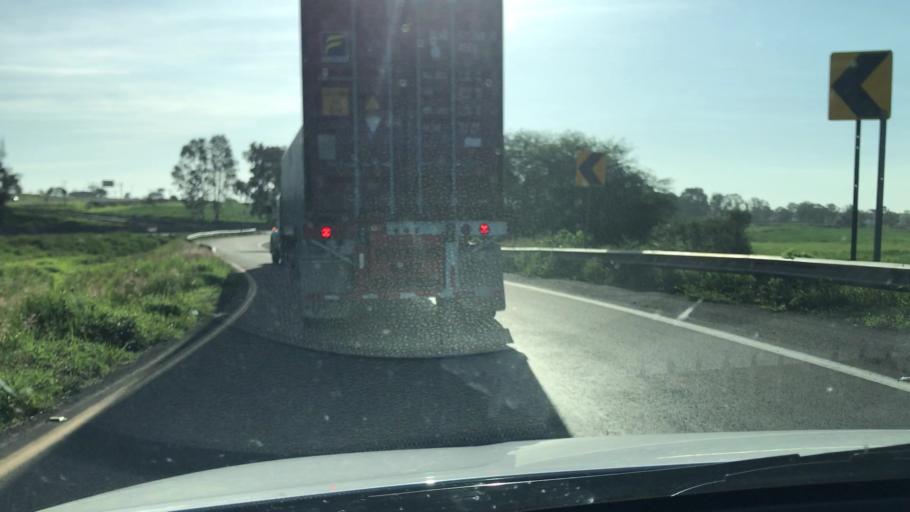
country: MX
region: Jalisco
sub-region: Lagos de Moreno
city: Cristeros [Fraccionamiento]
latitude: 21.3163
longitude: -102.0451
